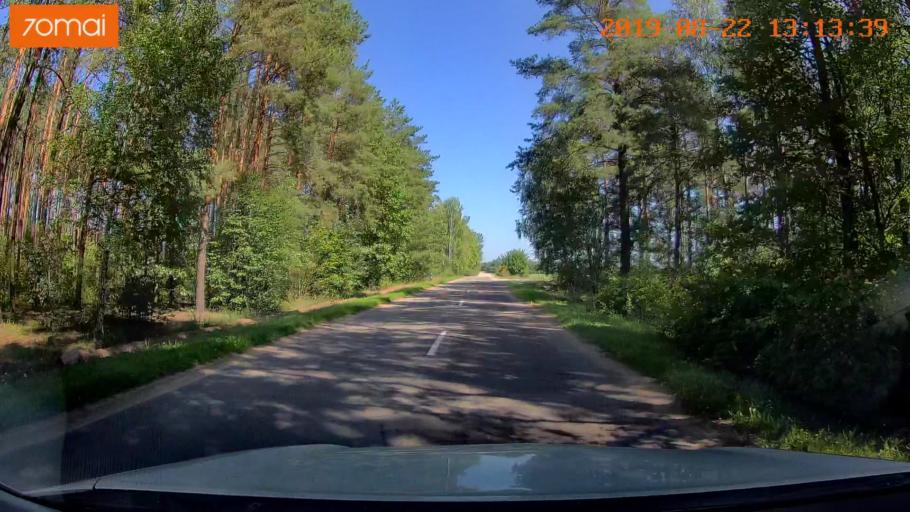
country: BY
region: Minsk
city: Prawdzinski
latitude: 53.2728
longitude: 27.8794
